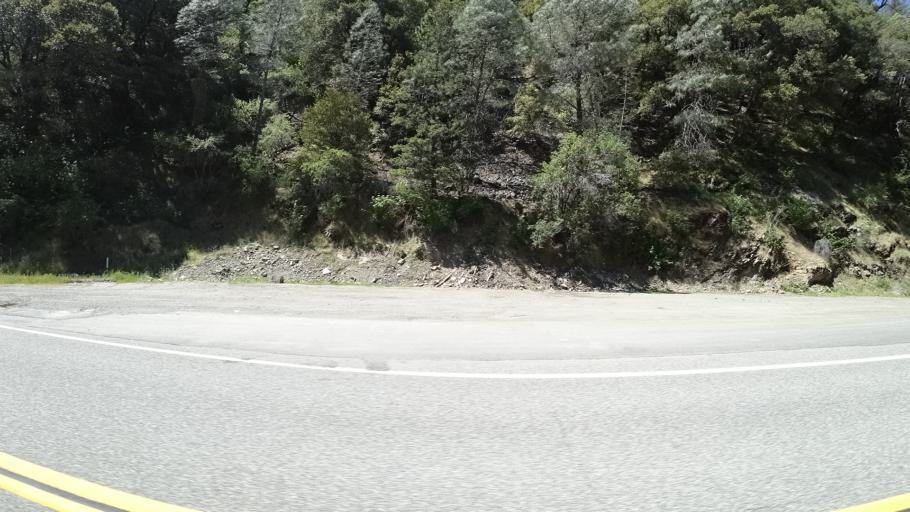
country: US
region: California
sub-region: Trinity County
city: Hayfork
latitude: 40.7533
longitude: -123.1576
